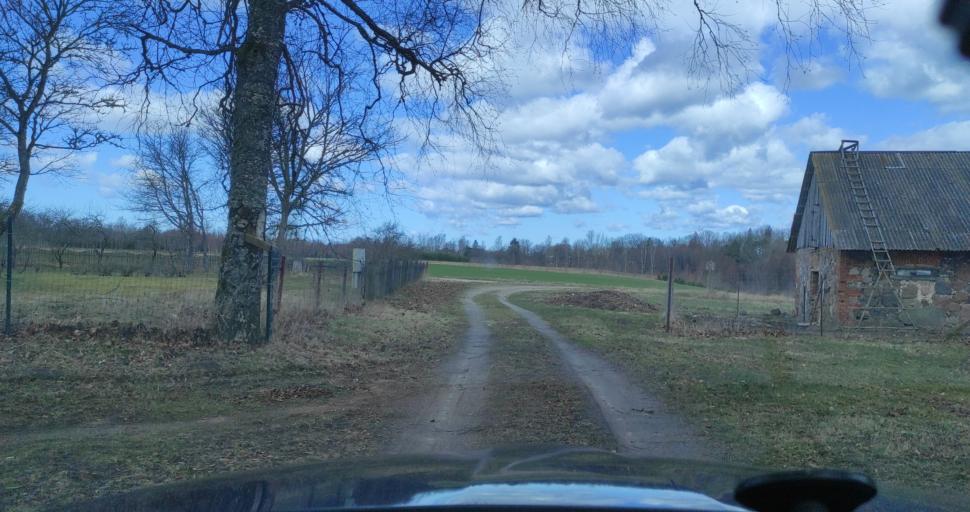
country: LV
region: Kuldigas Rajons
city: Kuldiga
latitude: 56.9574
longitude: 21.9180
